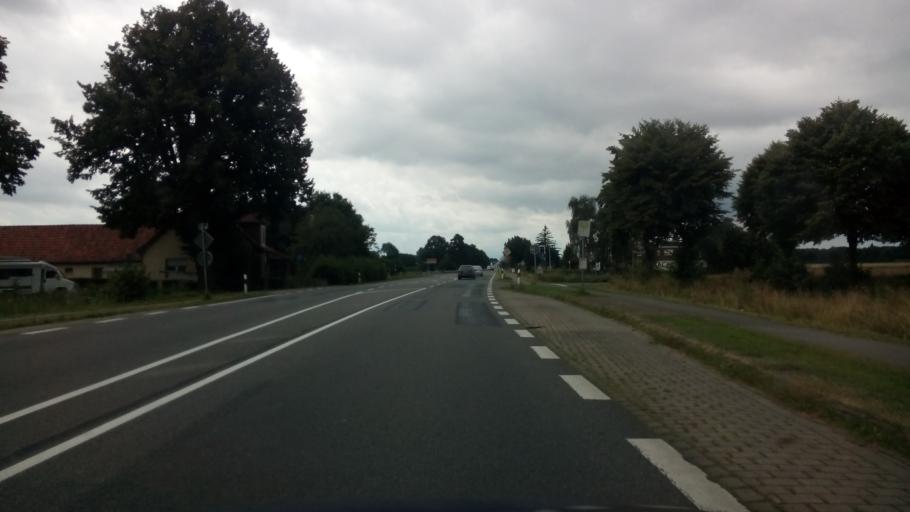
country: DE
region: Lower Saxony
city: Huede
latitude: 52.5088
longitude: 8.3756
